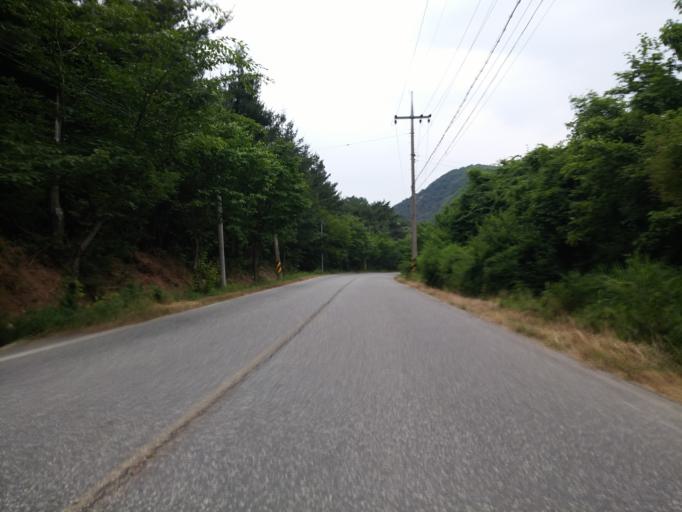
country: KR
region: Chungcheongbuk-do
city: Okcheon
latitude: 36.2019
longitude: 127.5702
